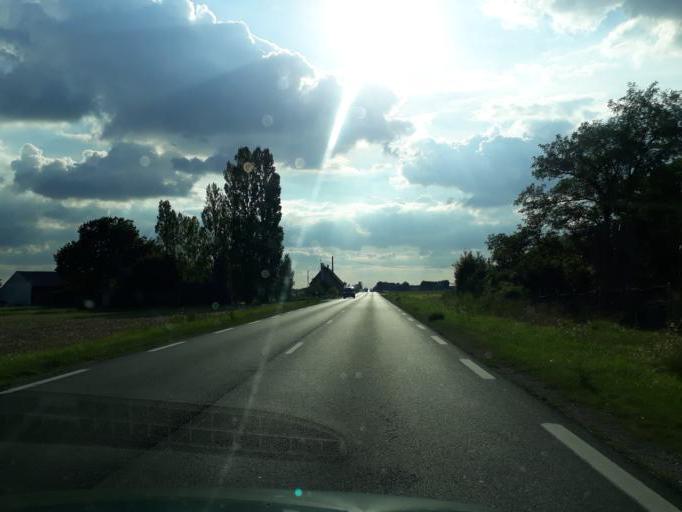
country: FR
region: Centre
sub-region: Departement du Loir-et-Cher
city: La Ville-aux-Clercs
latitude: 47.8919
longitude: 1.0670
